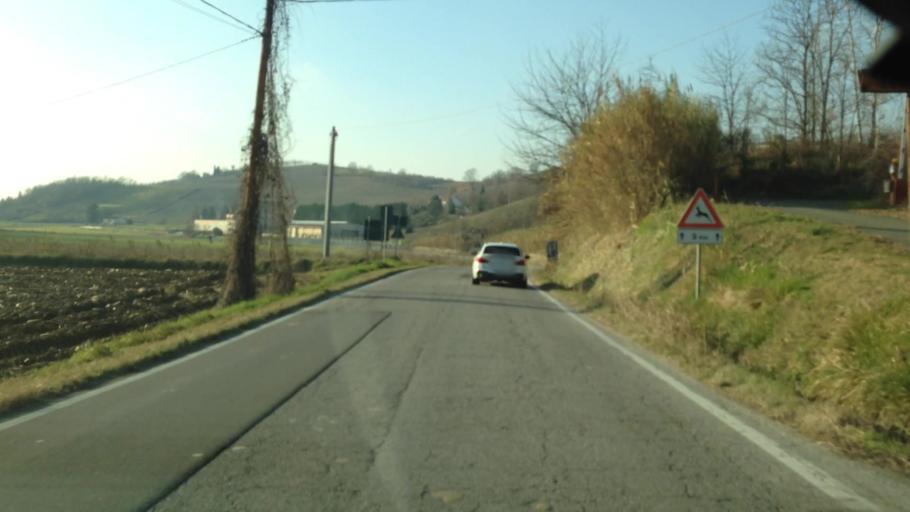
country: IT
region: Piedmont
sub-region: Provincia di Asti
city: Cortiglione
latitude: 44.8334
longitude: 8.3505
